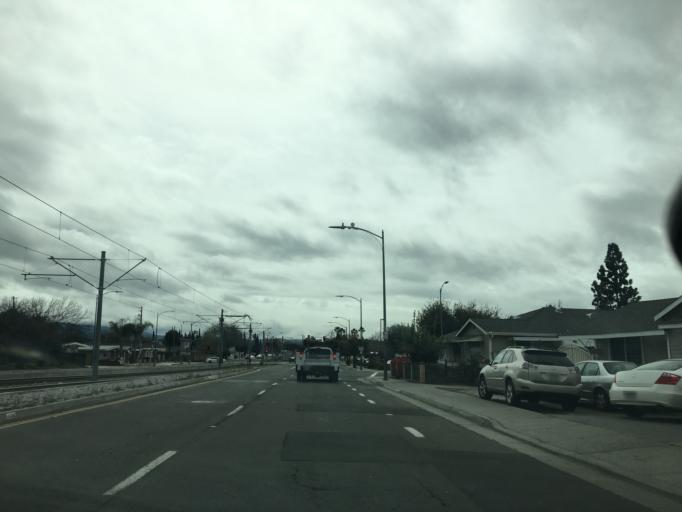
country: US
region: California
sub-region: Santa Clara County
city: Alum Rock
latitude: 37.3608
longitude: -121.8341
